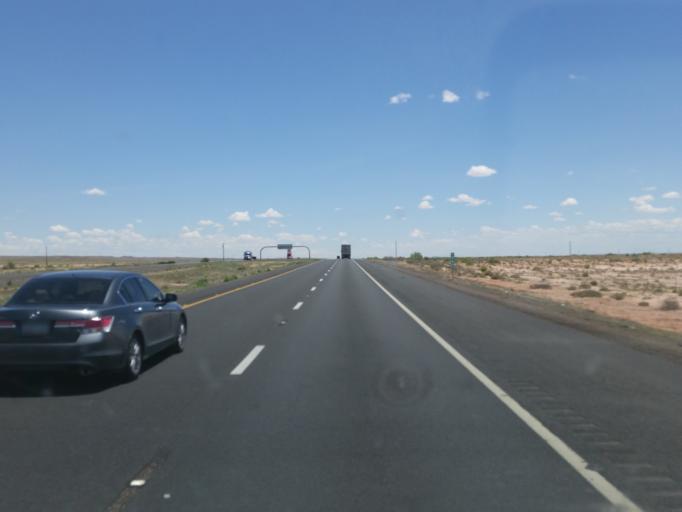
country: US
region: Arizona
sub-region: Navajo County
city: Winslow
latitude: 35.0017
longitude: -110.6037
